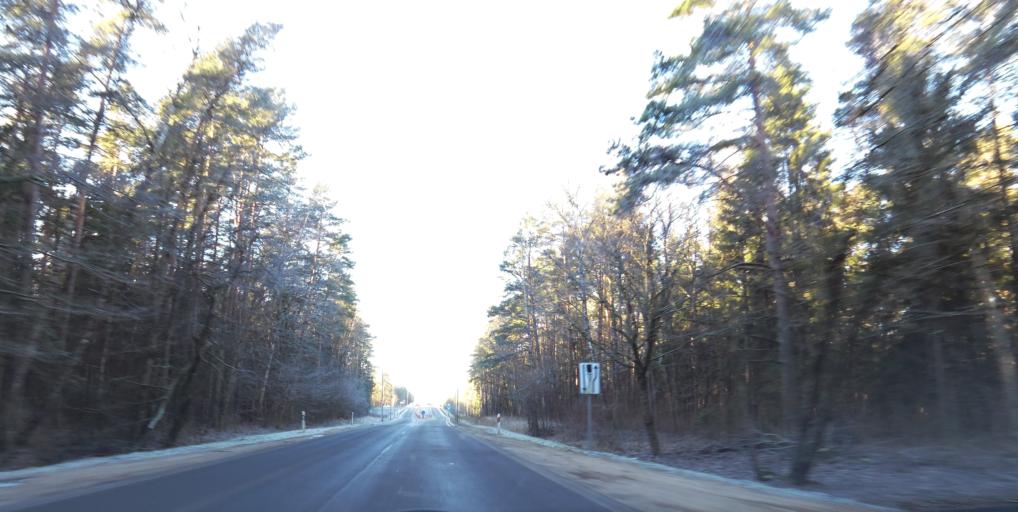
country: LT
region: Vilnius County
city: Lazdynai
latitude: 54.6440
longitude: 25.1567
